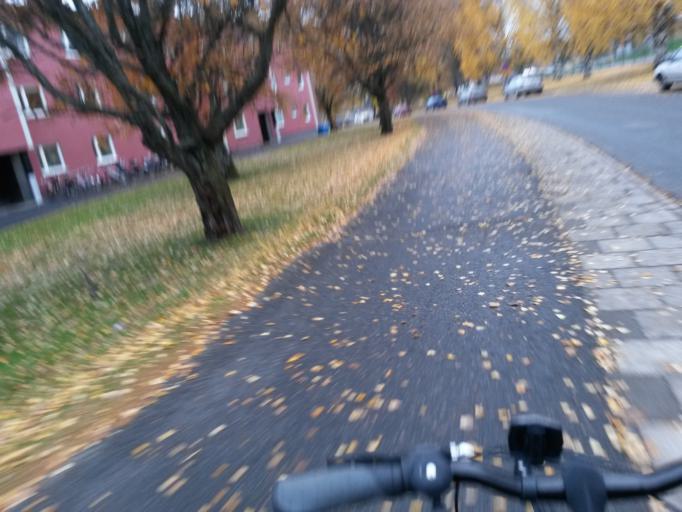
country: SE
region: Vaesterbotten
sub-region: Skelleftea Kommun
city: Skelleftea
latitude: 64.7594
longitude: 20.9705
